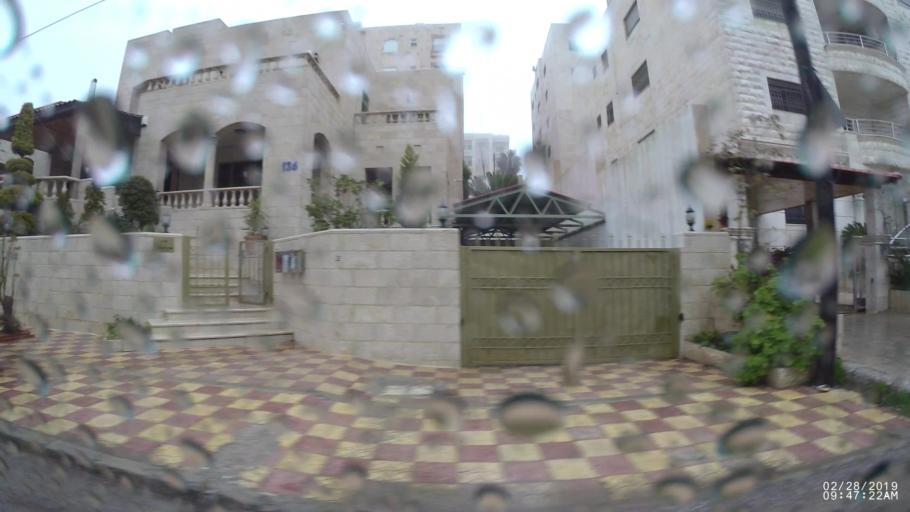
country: JO
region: Amman
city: Al Jubayhah
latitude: 32.0159
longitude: 35.8846
